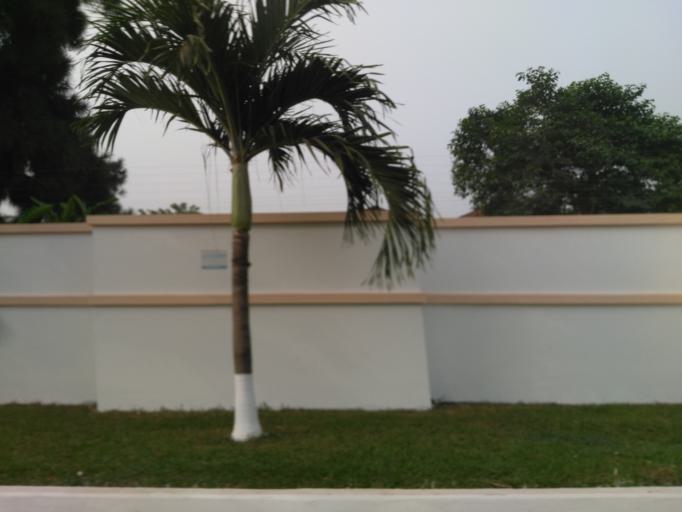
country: GH
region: Ashanti
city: Kumasi
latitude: 6.6553
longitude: -1.6222
